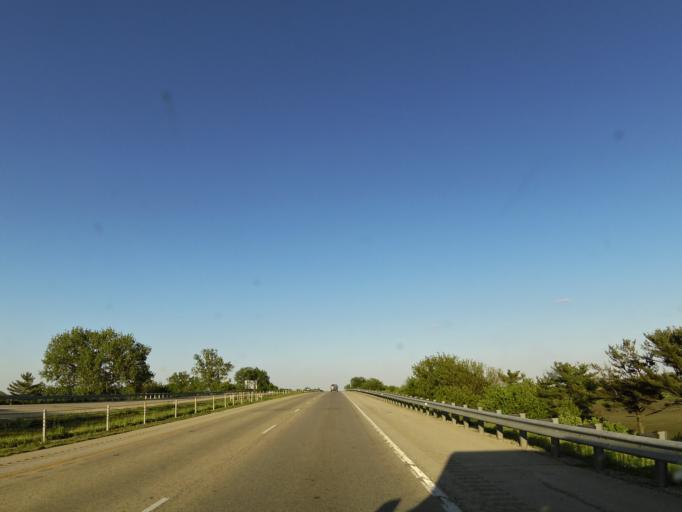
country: US
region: Illinois
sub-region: Champaign County
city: Saint Joseph
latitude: 40.1200
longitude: -88.0133
